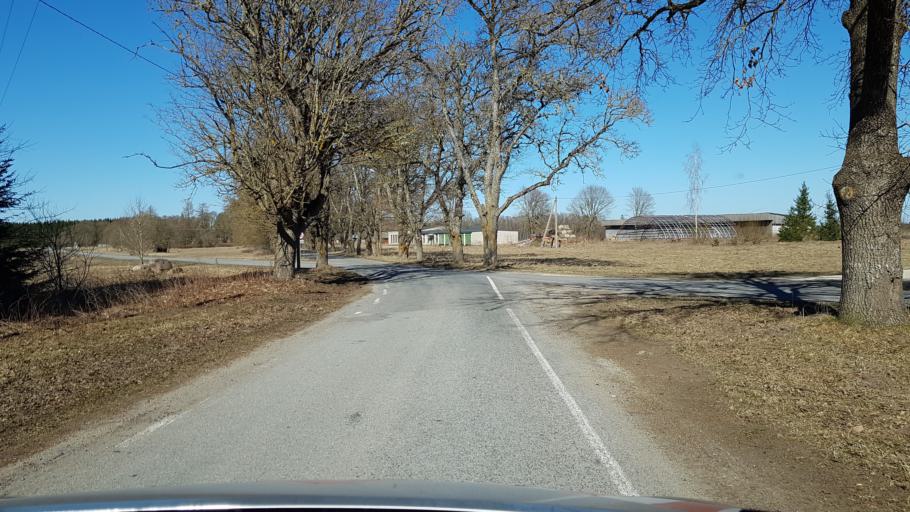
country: EE
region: Laeaene-Virumaa
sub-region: Viru-Nigula vald
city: Kunda
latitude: 59.4111
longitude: 26.5305
